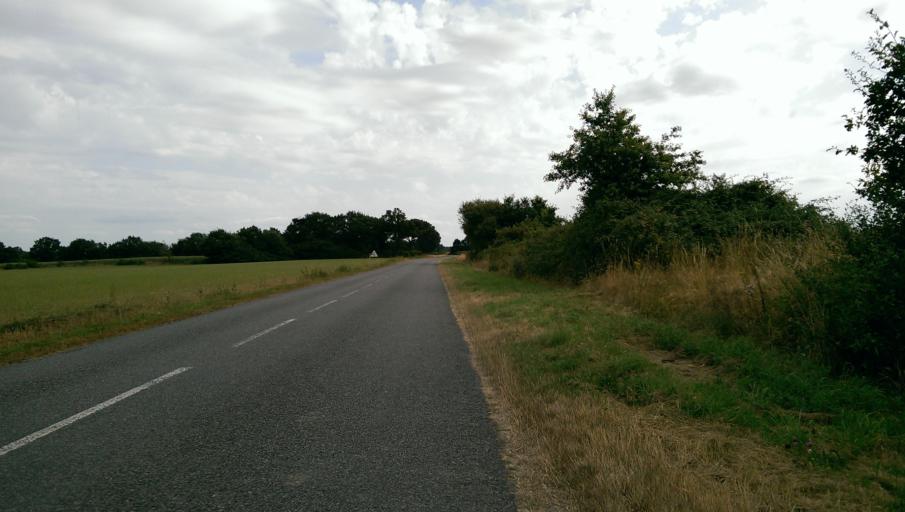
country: FR
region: Pays de la Loire
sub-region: Departement de la Loire-Atlantique
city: La Planche
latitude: 47.0008
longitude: -1.4303
